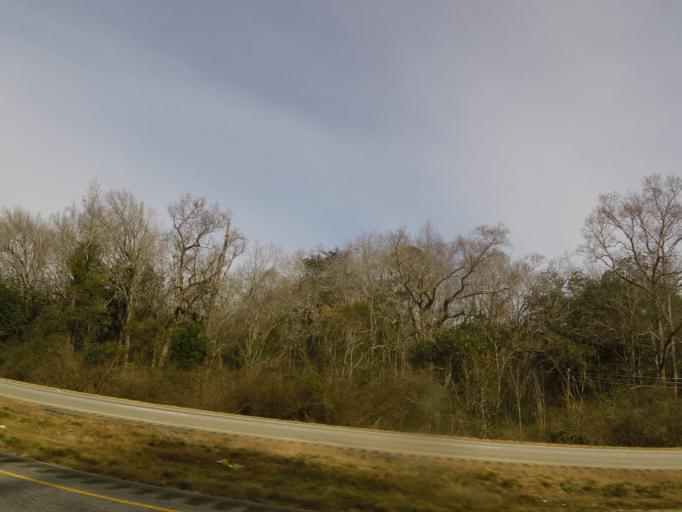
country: US
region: Alabama
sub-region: Dale County
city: Midland City
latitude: 31.2995
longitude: -85.4841
